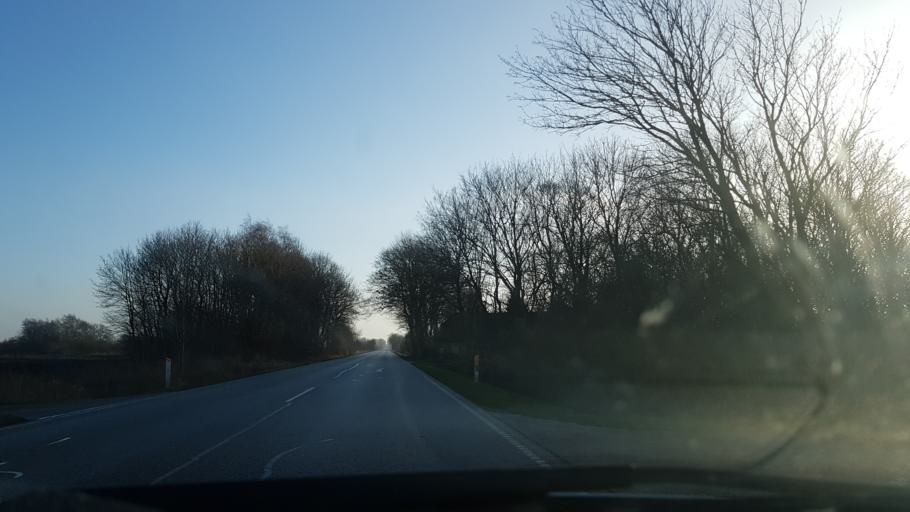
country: DK
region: South Denmark
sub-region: Tonder Kommune
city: Toftlund
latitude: 55.2356
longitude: 9.1642
